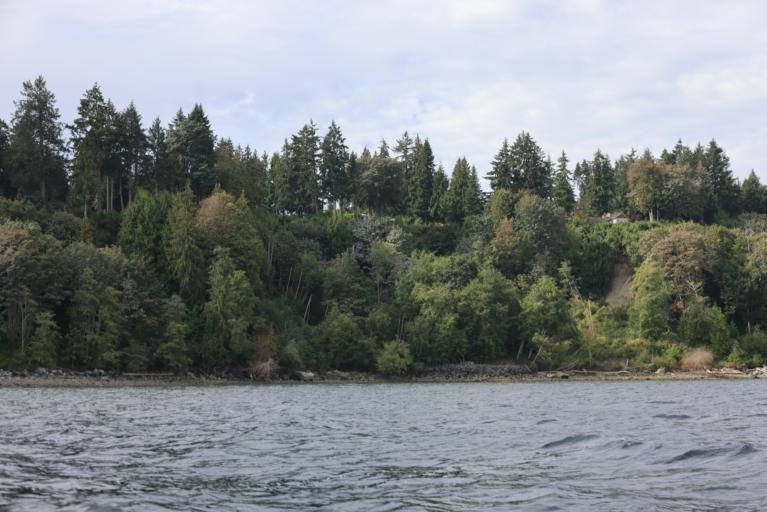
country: CA
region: British Columbia
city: Nanaimo
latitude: 49.2452
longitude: -124.0202
